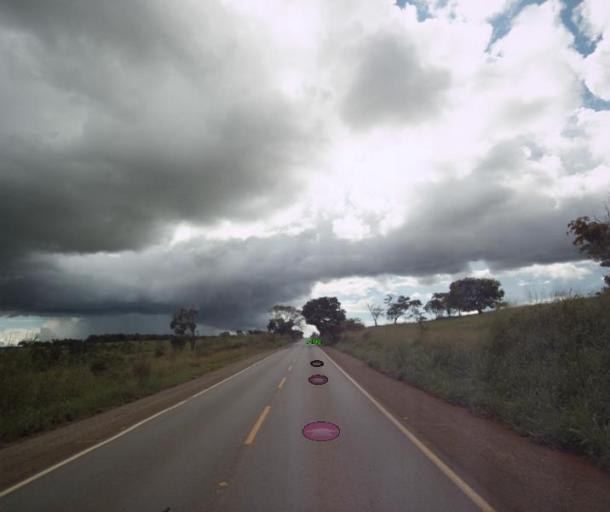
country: BR
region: Goias
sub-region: Uruacu
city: Uruacu
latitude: -14.6813
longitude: -49.1318
